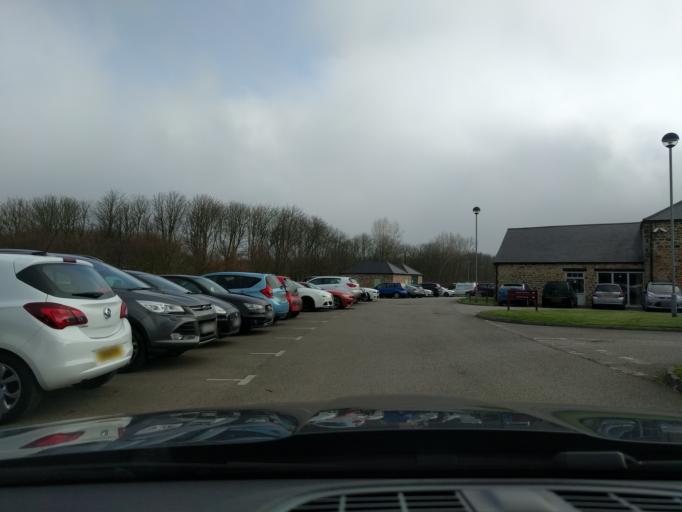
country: GB
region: England
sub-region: Sunderland
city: Washington
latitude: 54.8626
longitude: -1.5197
